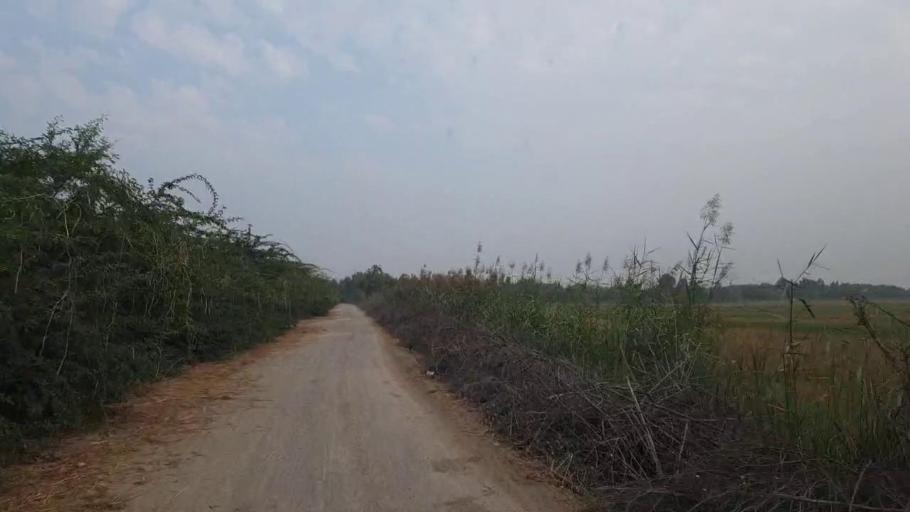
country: PK
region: Sindh
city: Talhar
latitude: 24.8314
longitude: 68.8805
